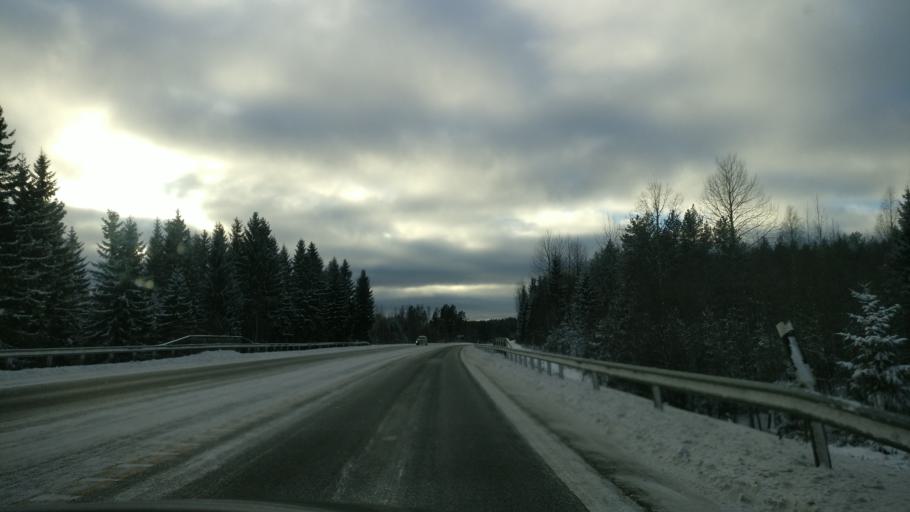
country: FI
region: Southern Savonia
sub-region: Mikkeli
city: Pertunmaa
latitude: 61.3737
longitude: 26.2953
